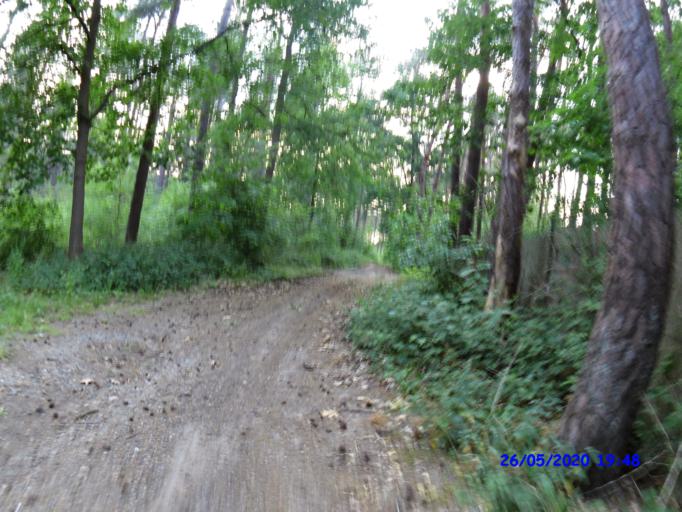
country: BE
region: Flanders
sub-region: Provincie Antwerpen
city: Herentals
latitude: 51.1722
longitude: 4.7951
